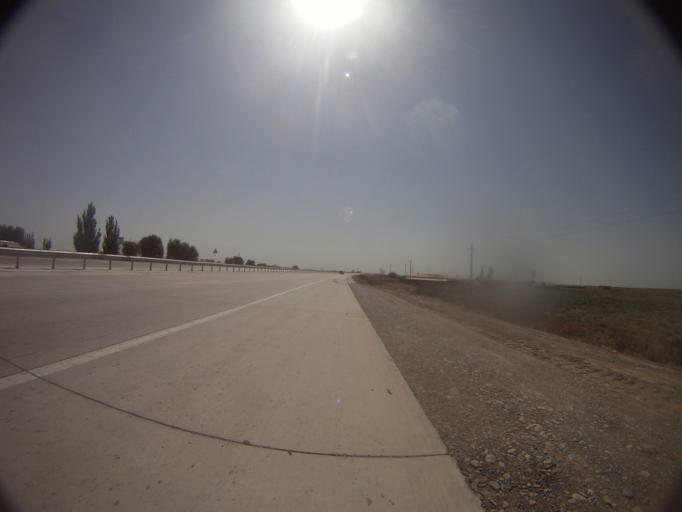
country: KZ
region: Ongtustik Qazaqstan
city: Turkestan
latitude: 43.1439
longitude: 68.5787
